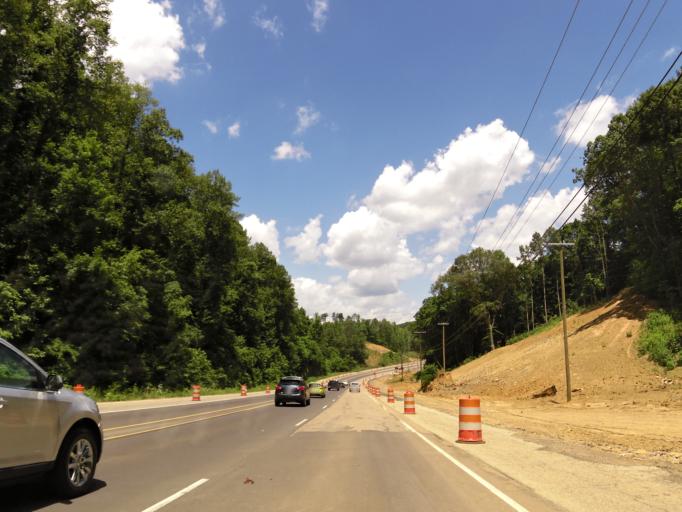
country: US
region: Tennessee
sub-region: Union County
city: Condon
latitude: 36.1528
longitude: -83.9131
